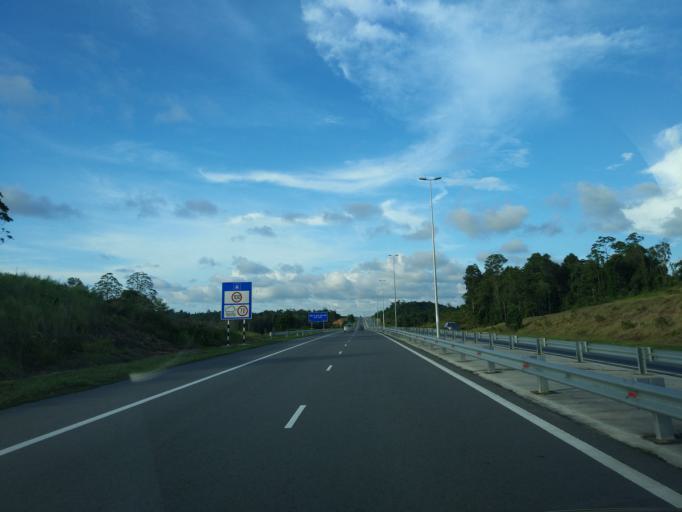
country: BN
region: Tutong
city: Tutong
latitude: 4.7013
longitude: 114.5710
